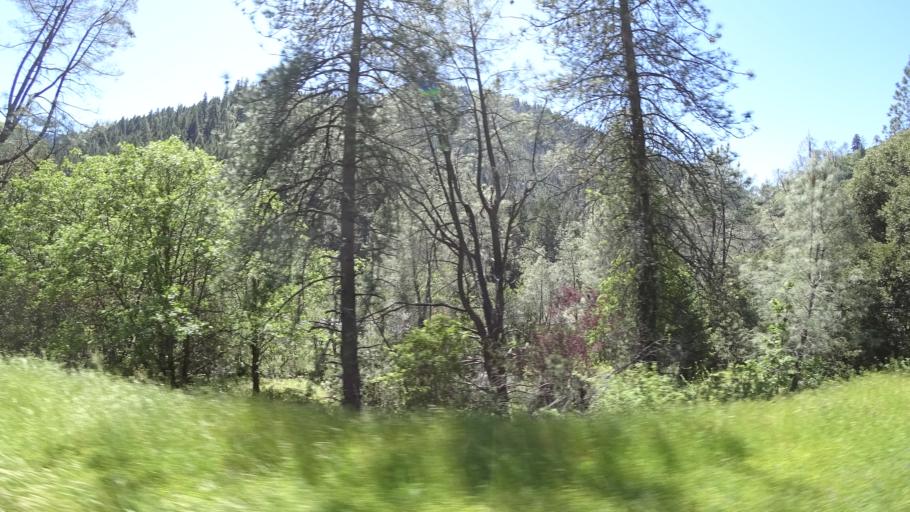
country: US
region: California
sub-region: Trinity County
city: Hayfork
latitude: 40.7933
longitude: -123.3524
